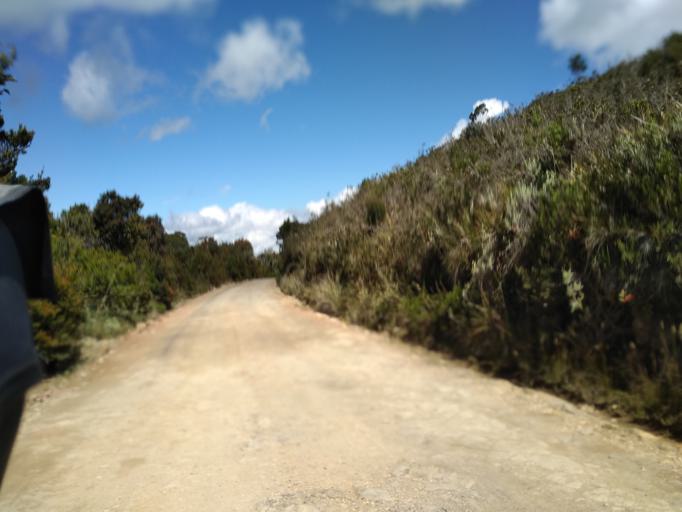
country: CO
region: Boyaca
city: Duitama
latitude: 5.9345
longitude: -73.0946
